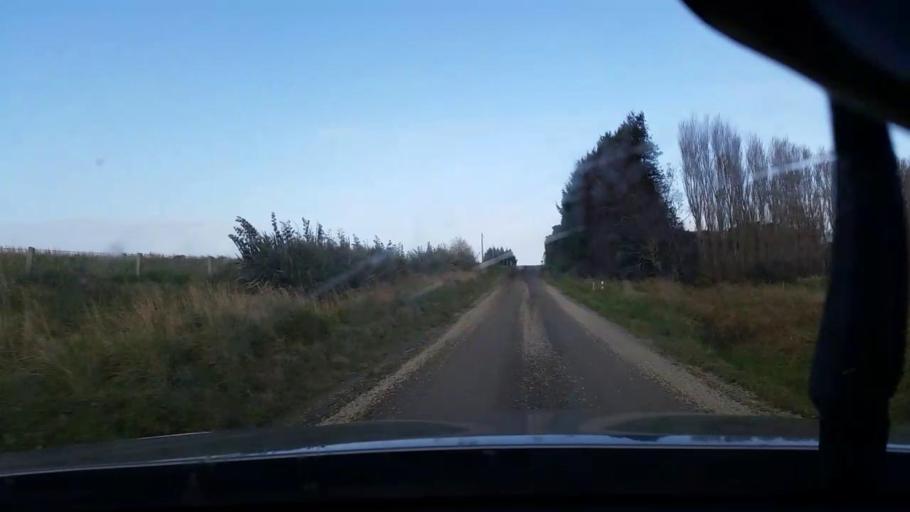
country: NZ
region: Southland
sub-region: Southland District
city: Winton
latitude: -46.2761
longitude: 168.2928
